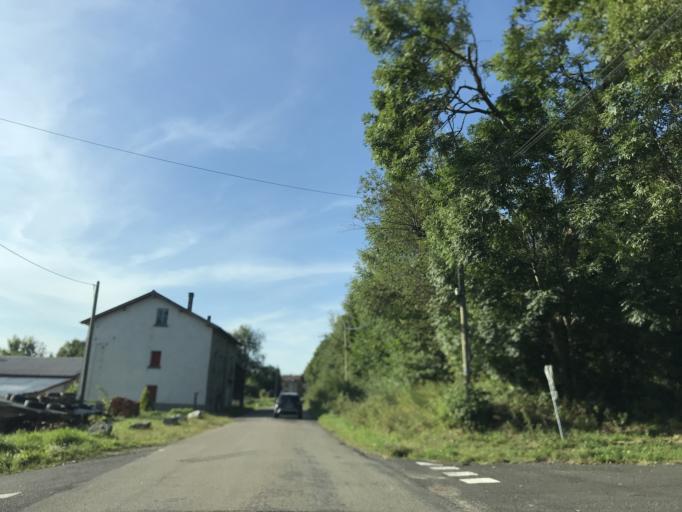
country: FR
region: Auvergne
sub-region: Departement du Puy-de-Dome
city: Job
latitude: 45.7042
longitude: 3.7219
